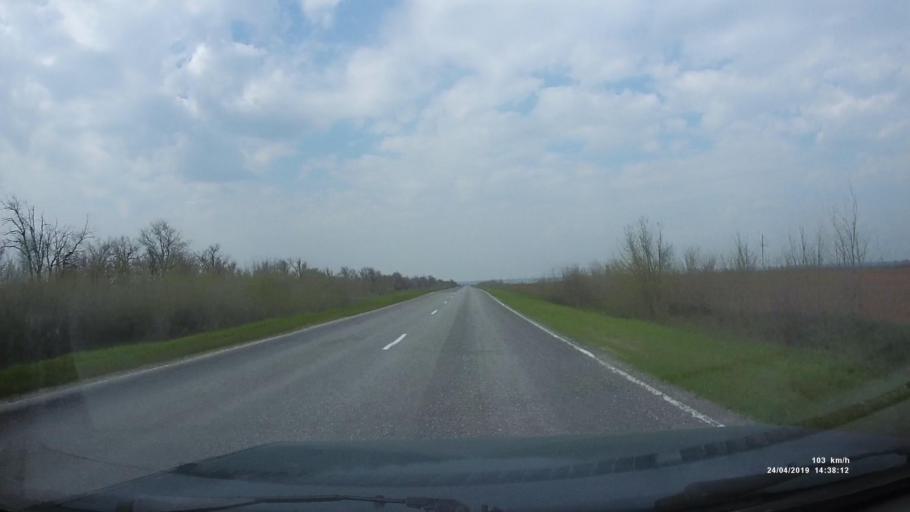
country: RU
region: Rostov
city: Remontnoye
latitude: 46.3980
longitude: 43.8861
